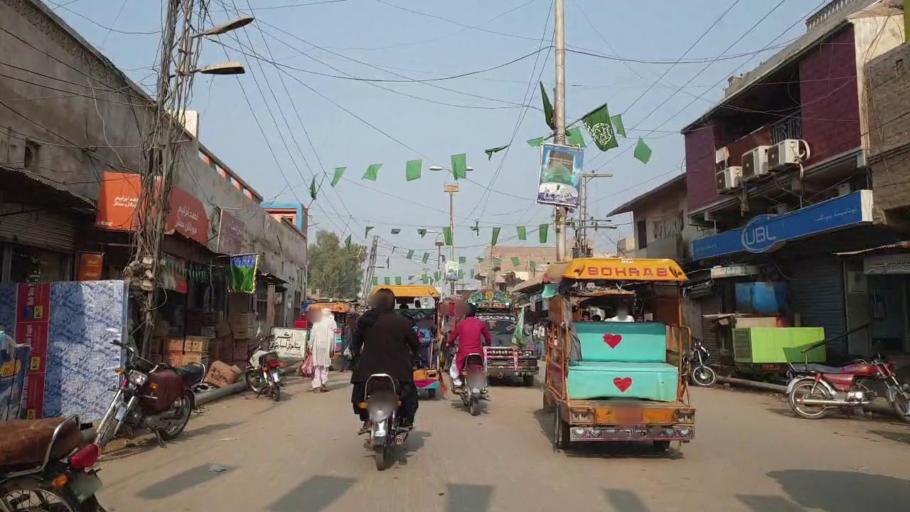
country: PK
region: Sindh
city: Bhan
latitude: 26.5591
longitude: 67.7212
